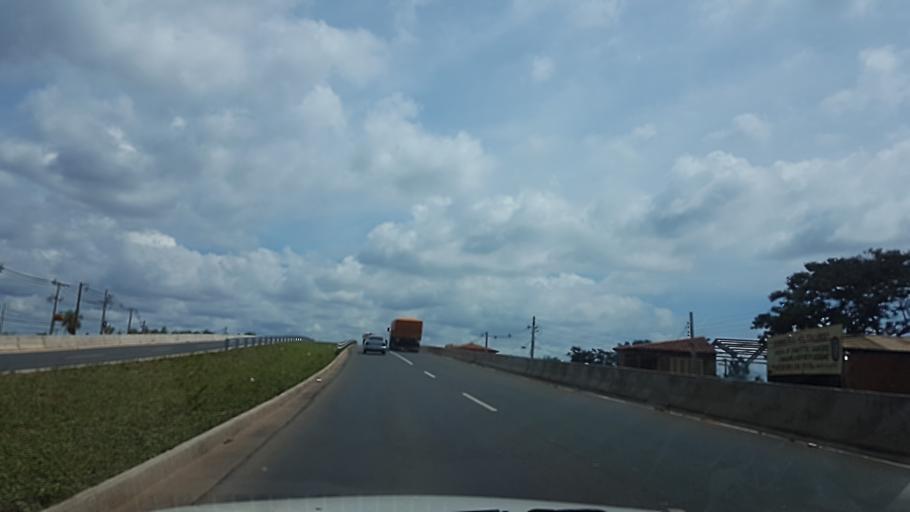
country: PY
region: Central
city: Limpio
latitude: -25.1829
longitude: -57.4926
